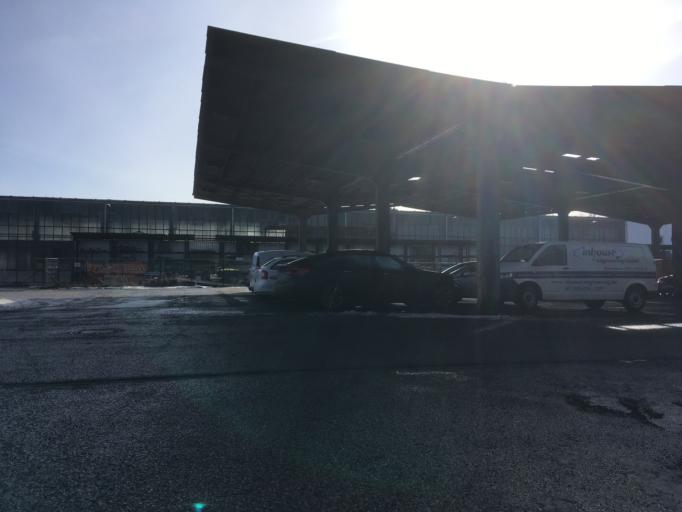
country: DE
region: Berlin
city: Kopenick Bezirk
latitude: 52.4693
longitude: 13.5618
